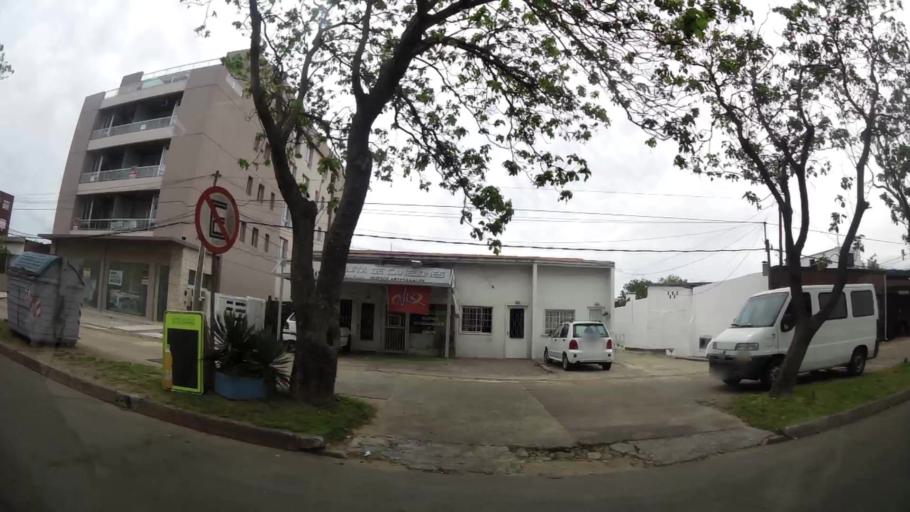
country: UY
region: Maldonado
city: Maldonado
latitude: -34.9060
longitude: -54.9634
